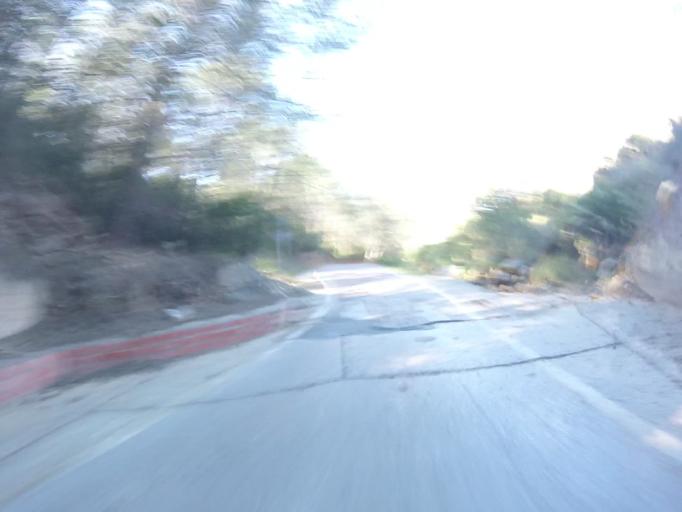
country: ES
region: Valencia
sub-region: Provincia de Castello
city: Orpesa/Oropesa del Mar
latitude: 40.0793
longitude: 0.1181
